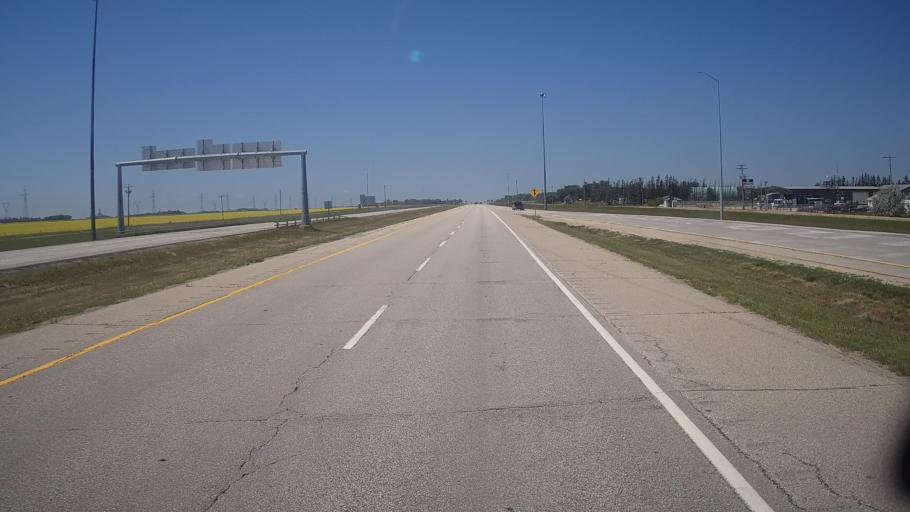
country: CA
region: Manitoba
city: Winnipeg
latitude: 49.9900
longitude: -97.2364
